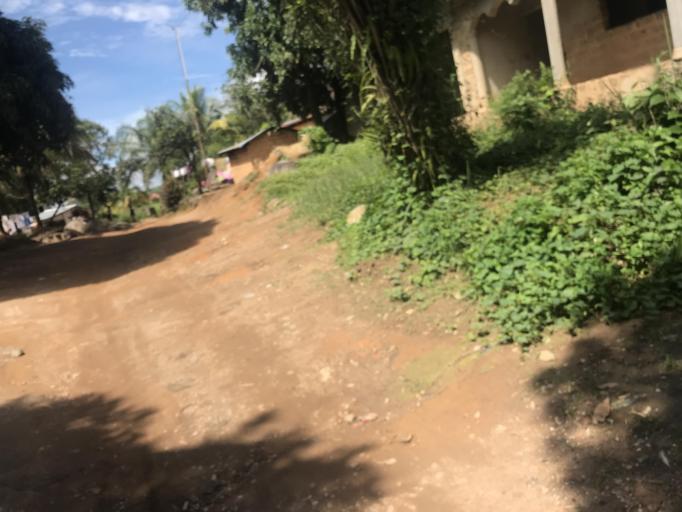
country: SL
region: Eastern Province
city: Koidu
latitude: 8.6461
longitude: -10.9888
